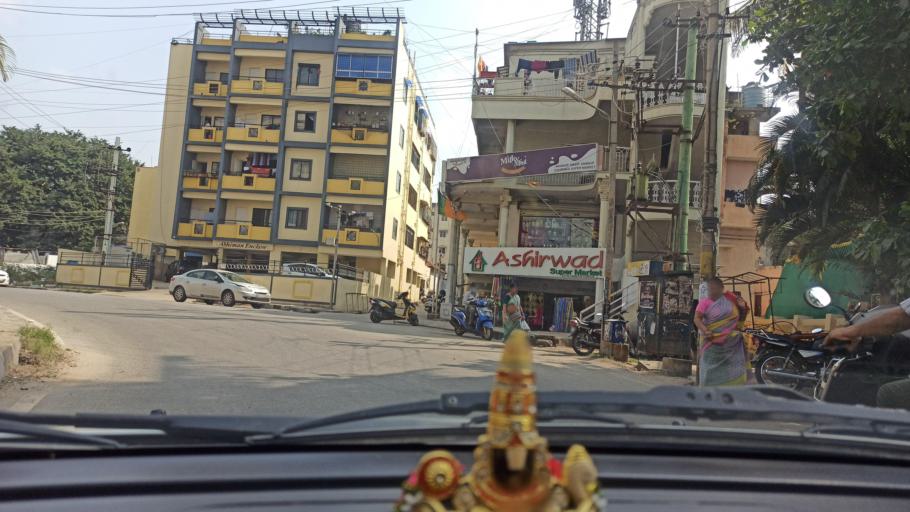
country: IN
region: Karnataka
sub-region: Bangalore Urban
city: Bangalore
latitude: 13.0136
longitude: 77.6501
